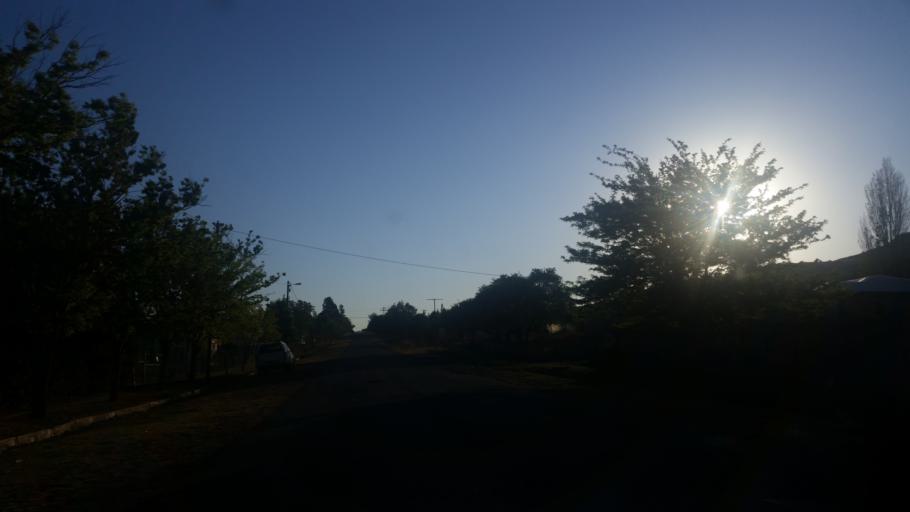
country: ZA
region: Orange Free State
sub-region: Thabo Mofutsanyana District Municipality
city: Phuthaditjhaba
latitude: -28.3149
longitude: 28.7005
